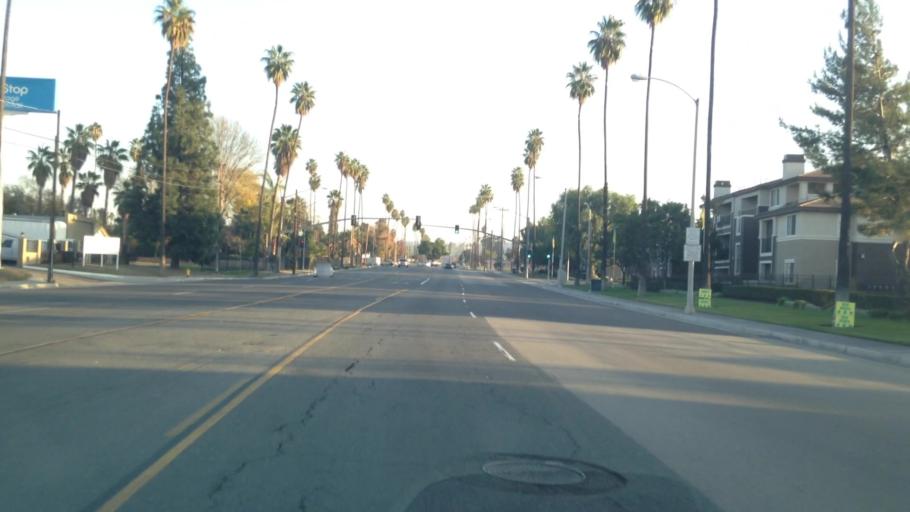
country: US
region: California
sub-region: Riverside County
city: Riverside
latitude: 33.9120
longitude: -117.4398
